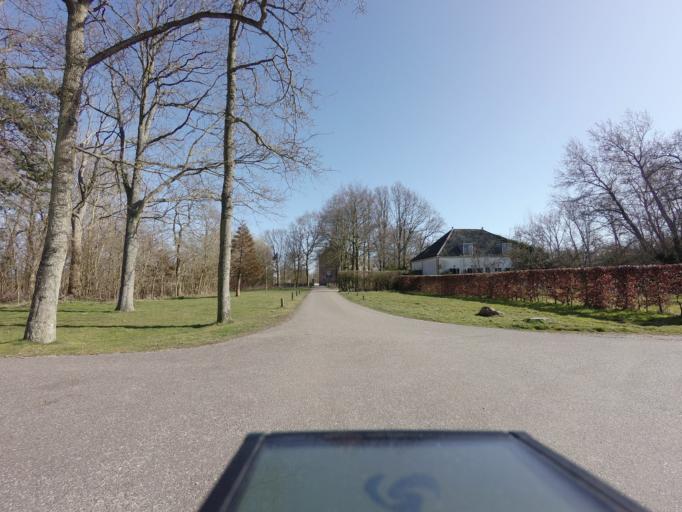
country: NL
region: Zeeland
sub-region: Schouwen-Duiveland
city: Renesse
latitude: 51.7342
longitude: 3.7852
